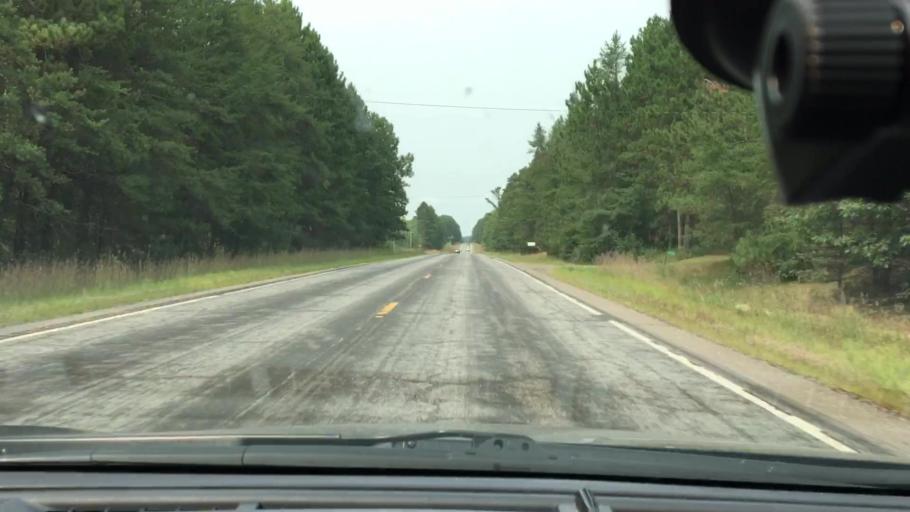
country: US
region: Minnesota
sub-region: Crow Wing County
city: Cross Lake
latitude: 46.7678
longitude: -93.9664
